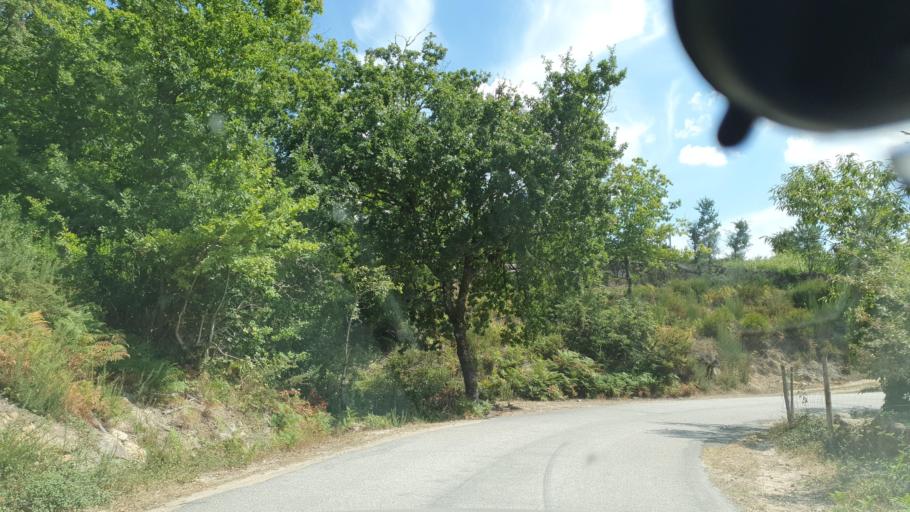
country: PT
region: Braga
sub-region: Vieira do Minho
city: Vieira do Minho
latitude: 41.7039
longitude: -8.0758
